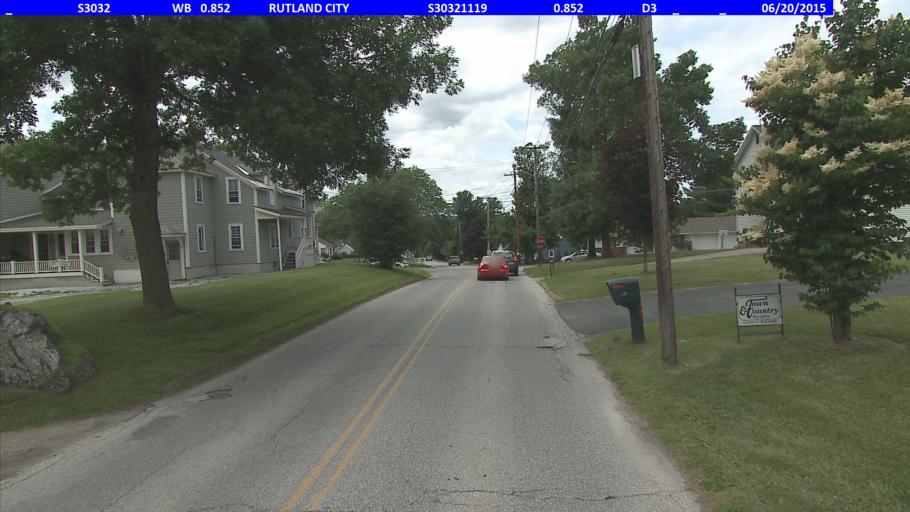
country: US
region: Vermont
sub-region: Rutland County
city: Rutland
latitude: 43.6078
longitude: -72.9556
